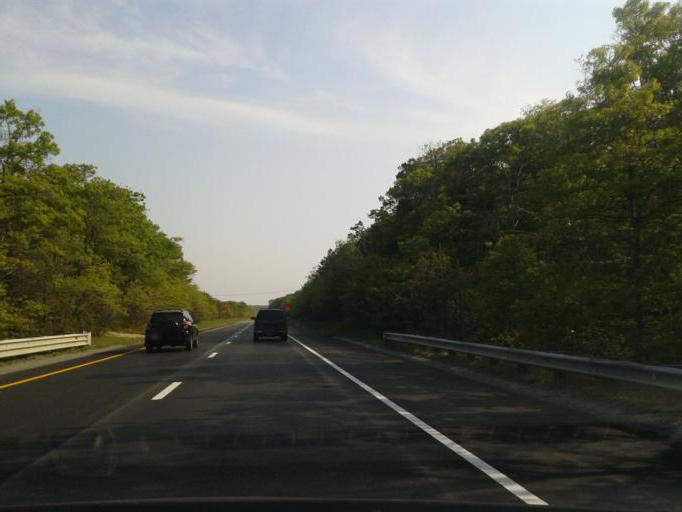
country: US
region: Massachusetts
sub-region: Barnstable County
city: North Falmouth
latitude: 41.6567
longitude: -70.6020
